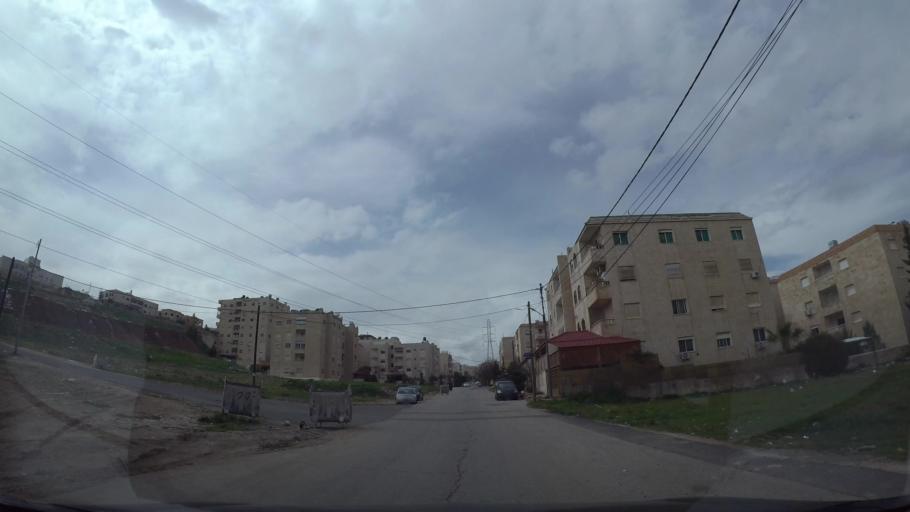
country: JO
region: Amman
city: Amman
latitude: 31.9951
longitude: 35.9396
